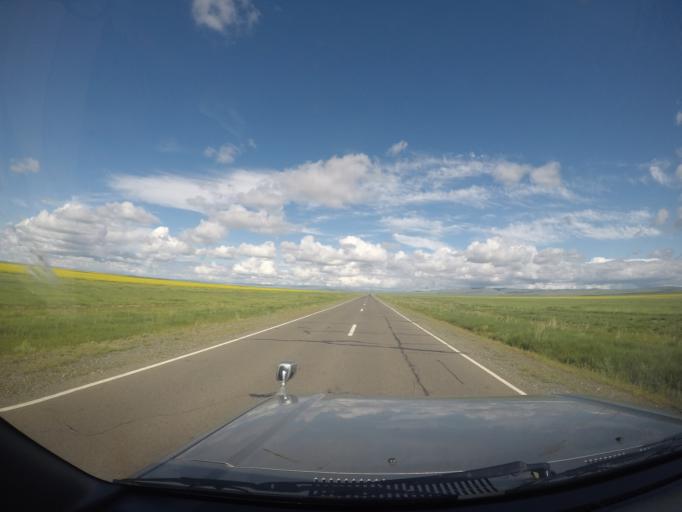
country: MN
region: Hentiy
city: Moron
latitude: 47.4185
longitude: 109.9424
